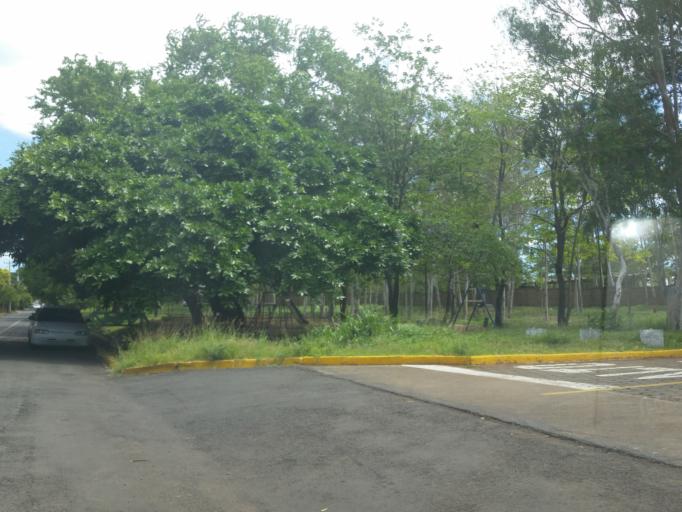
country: NI
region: Managua
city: Managua
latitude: 12.1207
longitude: -86.2859
